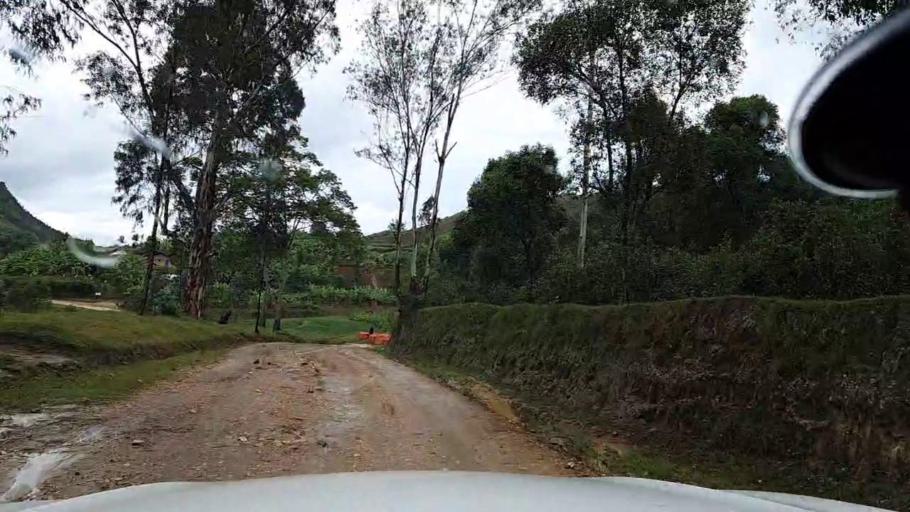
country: RW
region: Western Province
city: Kibuye
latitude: -2.1196
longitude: 29.4932
